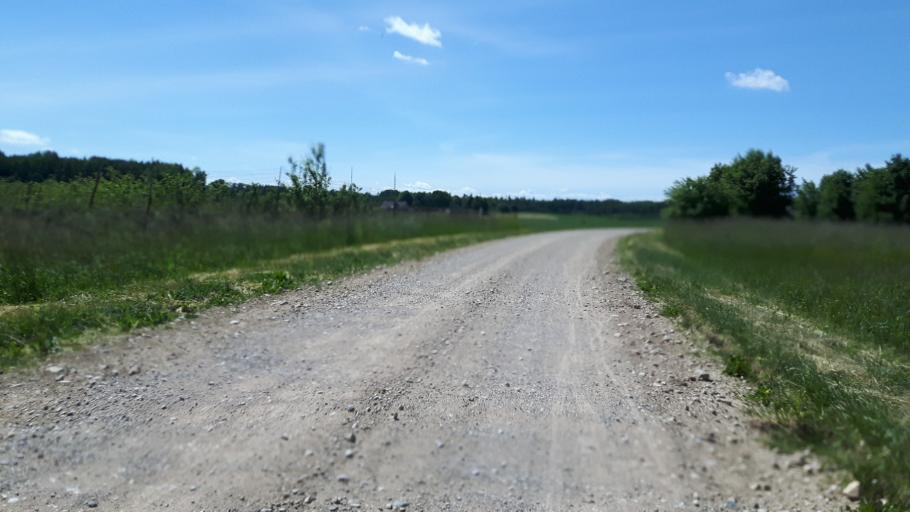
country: LV
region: Kandava
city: Kandava
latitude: 57.0424
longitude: 22.8661
